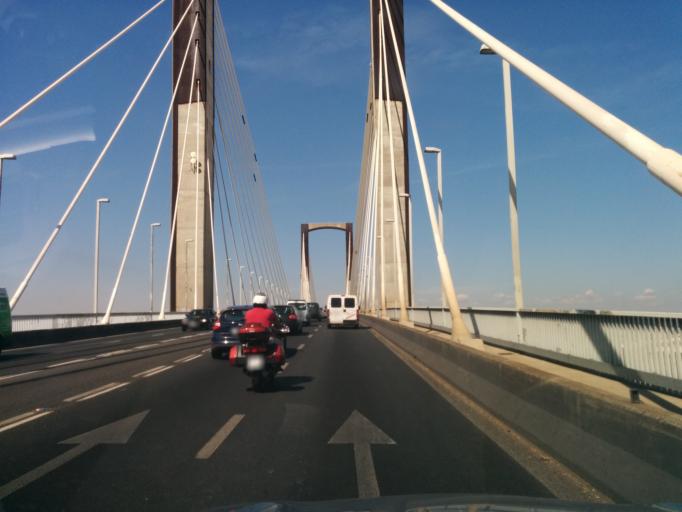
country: ES
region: Andalusia
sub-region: Provincia de Sevilla
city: Gelves
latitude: 37.3477
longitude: -5.9915
